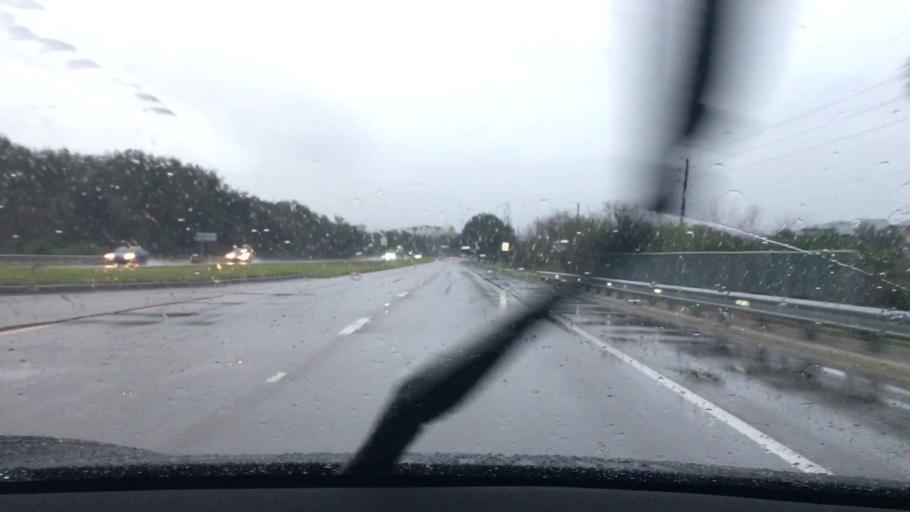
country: US
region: Florida
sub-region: Hillsborough County
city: Palm River-Clair Mel
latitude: 27.9343
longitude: -82.3379
